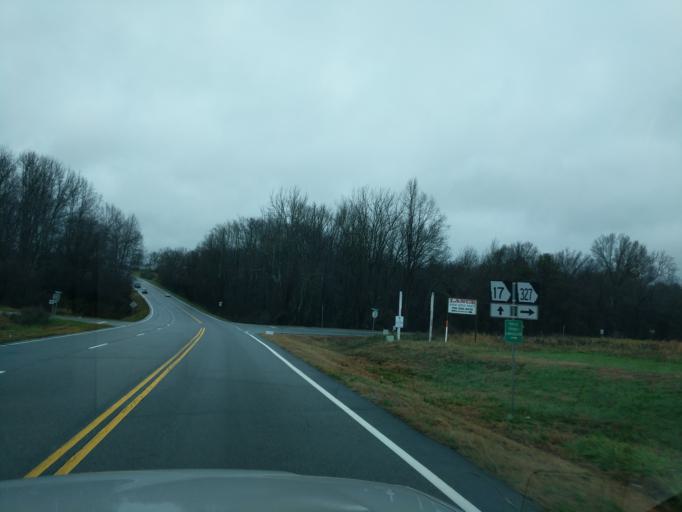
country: US
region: Georgia
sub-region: Franklin County
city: Lavonia
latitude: 34.3958
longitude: -83.1040
